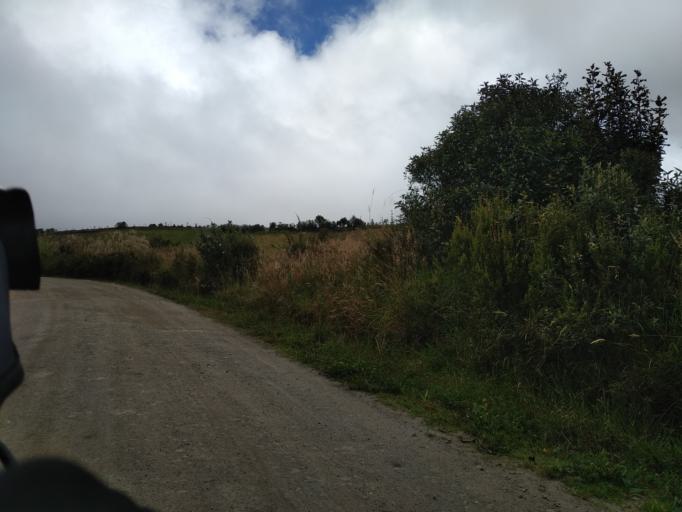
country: EC
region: Carchi
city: Tulcan
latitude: 0.7417
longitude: -77.7841
